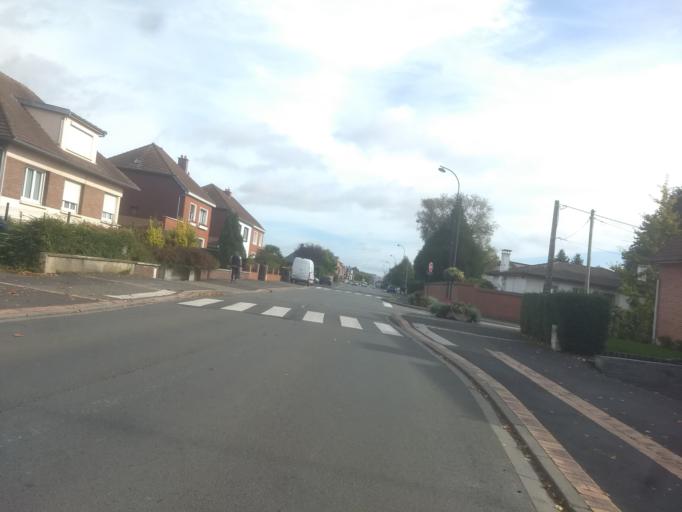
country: FR
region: Nord-Pas-de-Calais
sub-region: Departement du Pas-de-Calais
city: Dainville
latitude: 50.2839
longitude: 2.7356
